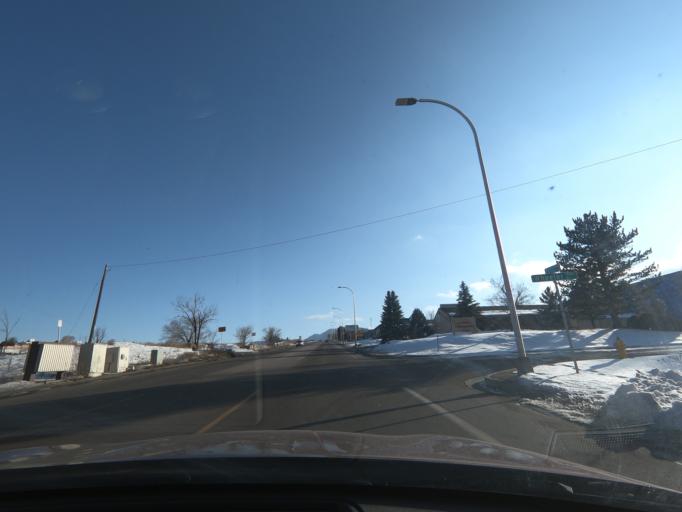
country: US
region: Colorado
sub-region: El Paso County
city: Colorado Springs
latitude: 38.8356
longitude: -104.8592
